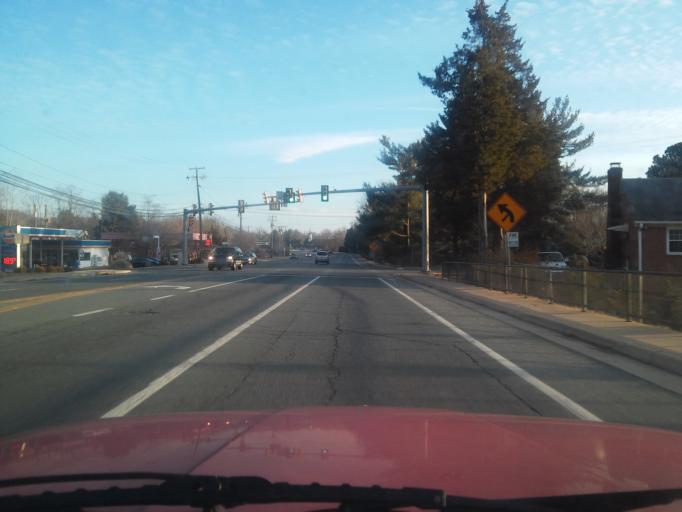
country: US
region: Virginia
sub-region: City of Charlottesville
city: Charlottesville
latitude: 38.0675
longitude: -78.4668
